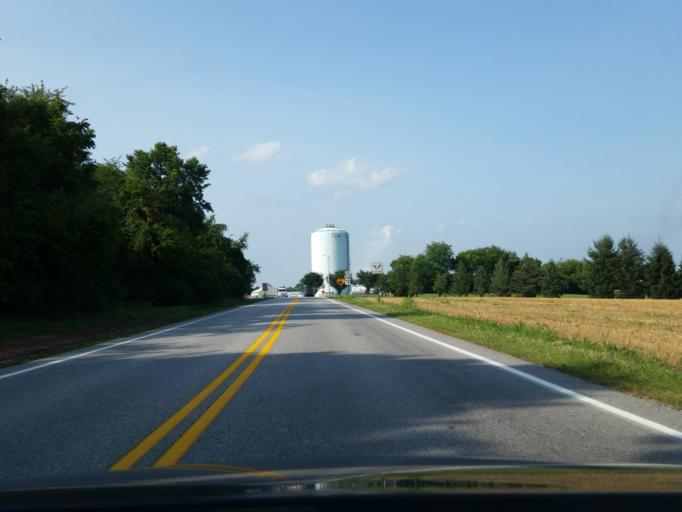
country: US
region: Pennsylvania
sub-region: York County
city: Emigsville
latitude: 40.0181
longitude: -76.7512
